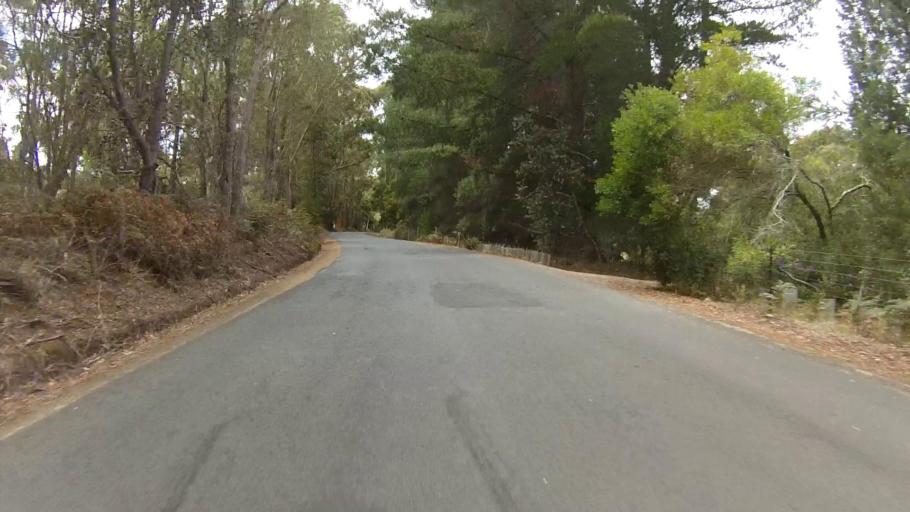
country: AU
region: Tasmania
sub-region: Kingborough
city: Margate
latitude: -43.0093
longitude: 147.2820
